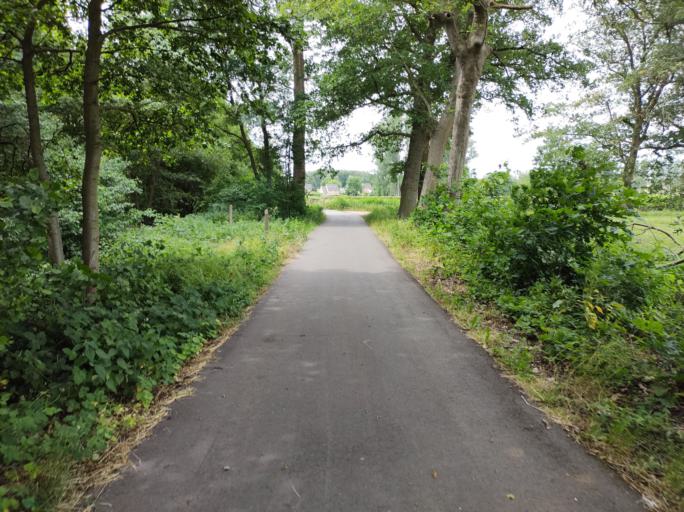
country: BE
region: Flanders
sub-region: Provincie Limburg
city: Diepenbeek
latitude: 50.9220
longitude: 5.4052
